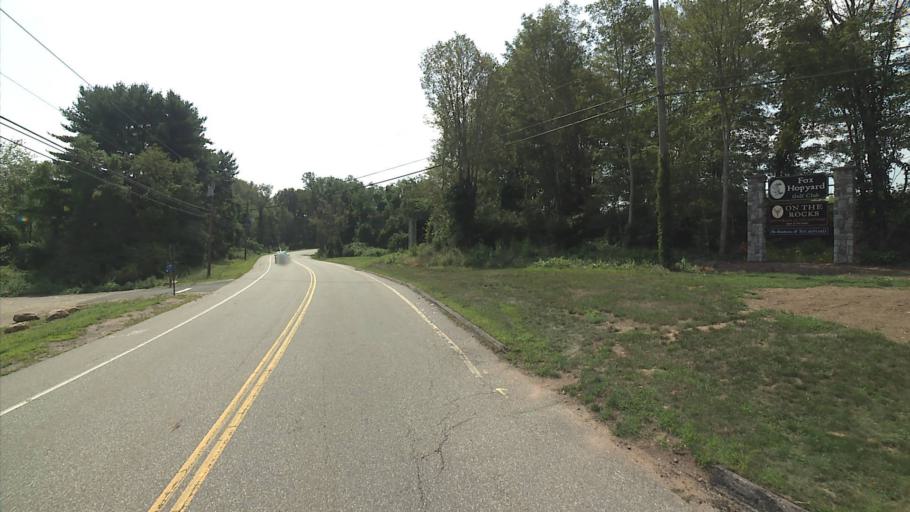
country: US
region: Connecticut
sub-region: Middlesex County
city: Essex Village
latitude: 41.4378
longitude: -72.3383
